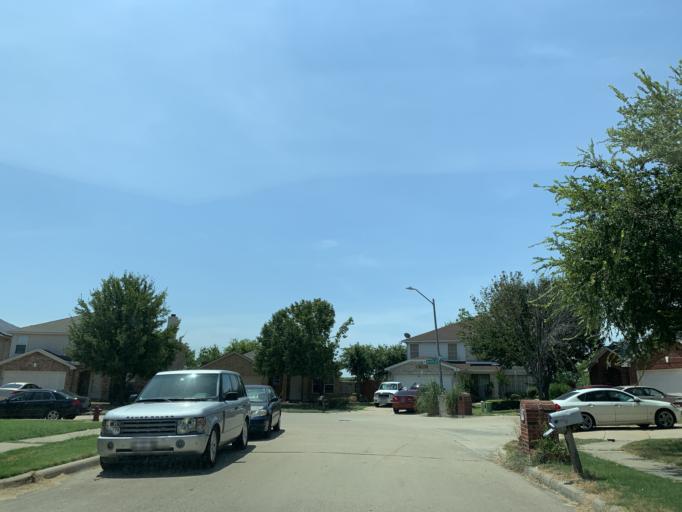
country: US
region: Texas
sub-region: Dallas County
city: Cedar Hill
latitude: 32.6407
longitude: -97.0369
